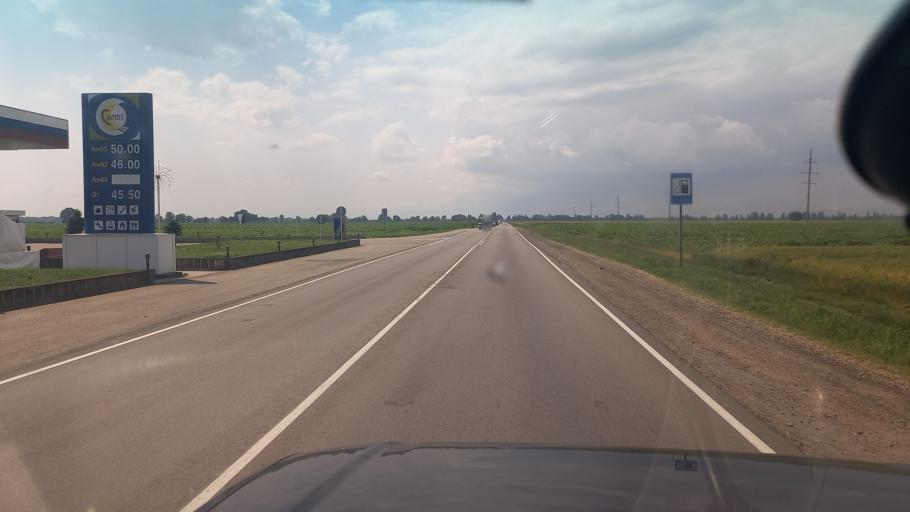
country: RU
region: Adygeya
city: Koshekhabl'
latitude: 44.9038
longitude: 40.4702
